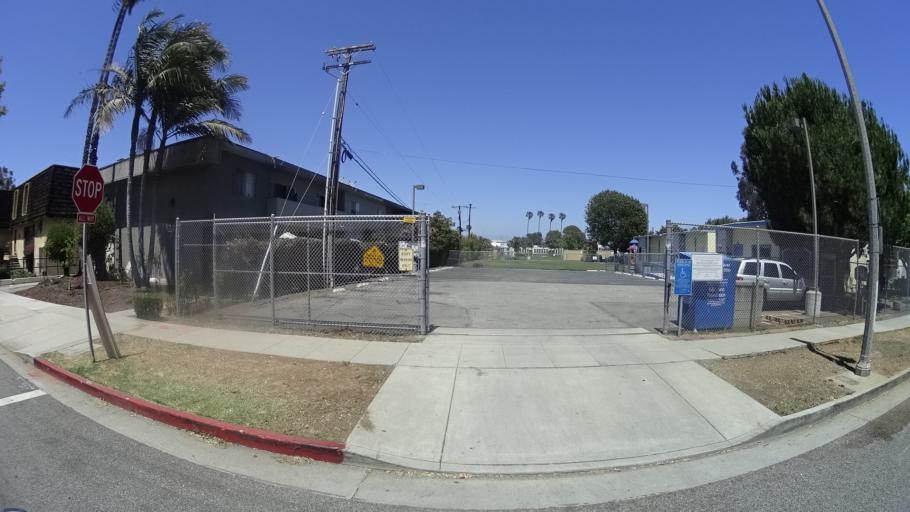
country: US
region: California
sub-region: Los Angeles County
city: Santa Monica
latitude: 34.0125
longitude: -118.4723
